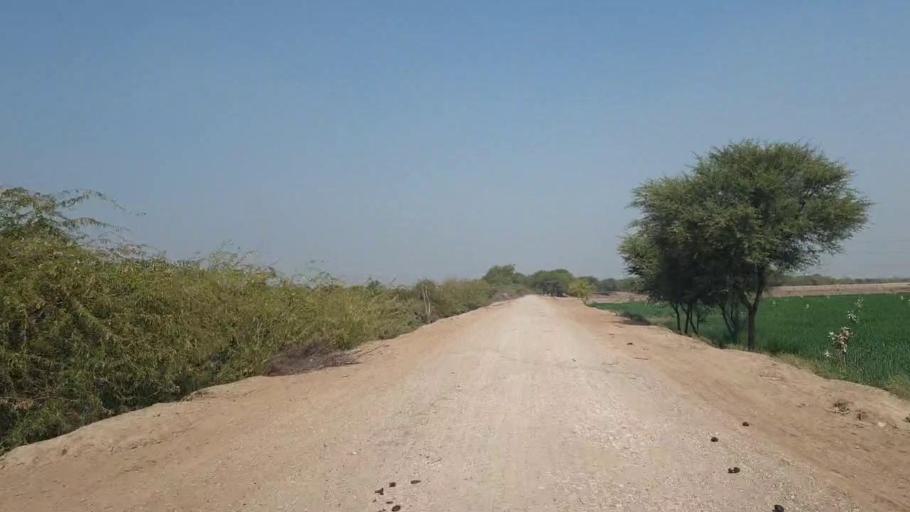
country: PK
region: Sindh
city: Chambar
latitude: 25.3493
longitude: 68.9156
